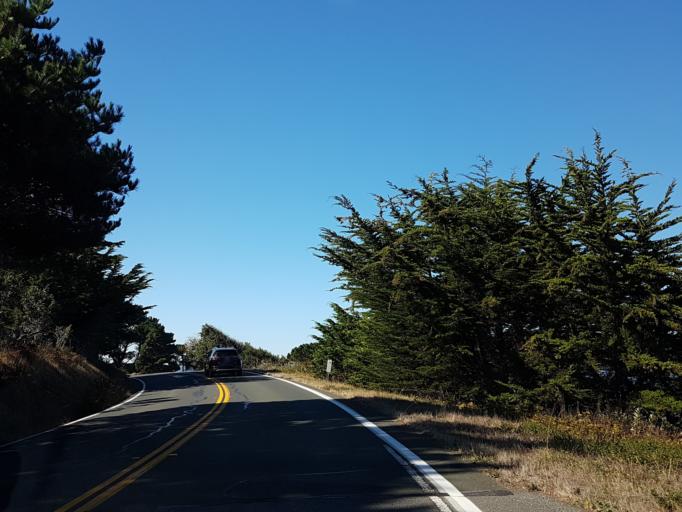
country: US
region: California
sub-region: Mendocino County
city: Boonville
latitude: 39.0196
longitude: -123.6871
